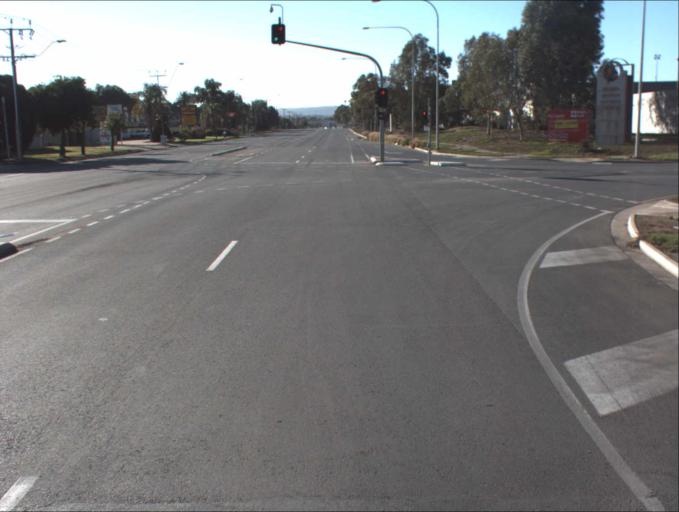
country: AU
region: South Australia
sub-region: Port Adelaide Enfield
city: Blair Athol
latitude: -34.8404
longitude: 138.5695
